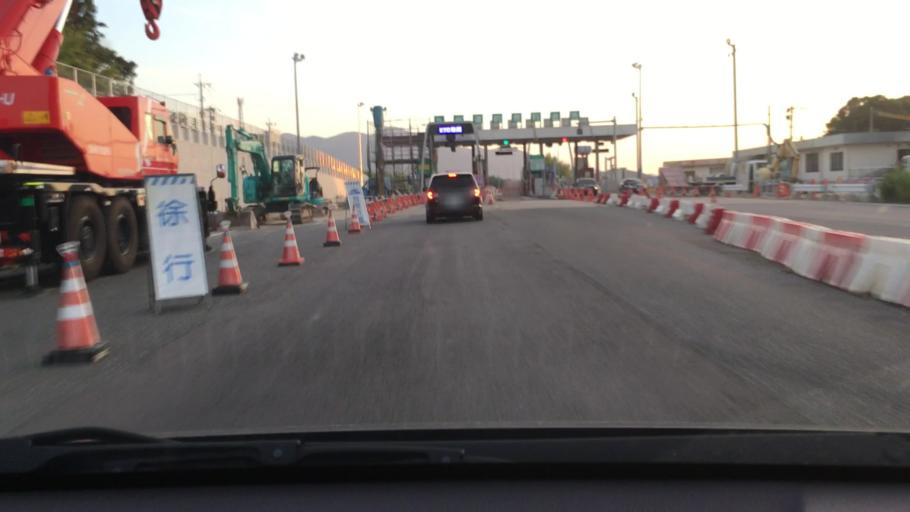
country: JP
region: Fukuoka
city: Maebaru-chuo
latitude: 33.5428
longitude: 130.2028
